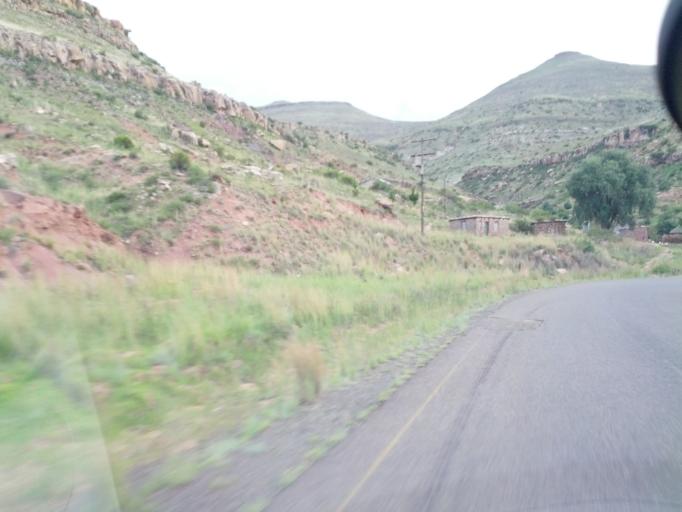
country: LS
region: Qacha's Nek
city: Qacha's Nek
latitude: -30.0673
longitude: 28.5342
